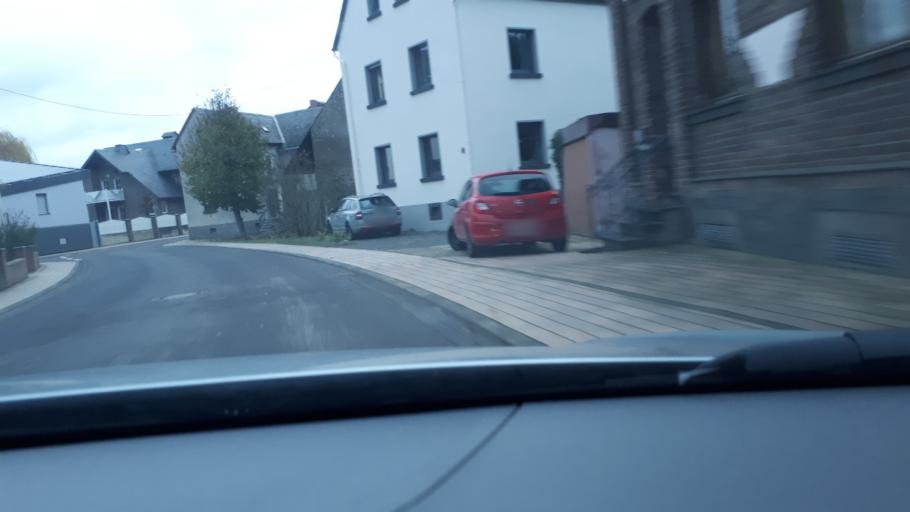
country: DE
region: Rheinland-Pfalz
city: Kehrig
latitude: 50.2801
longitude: 7.2234
